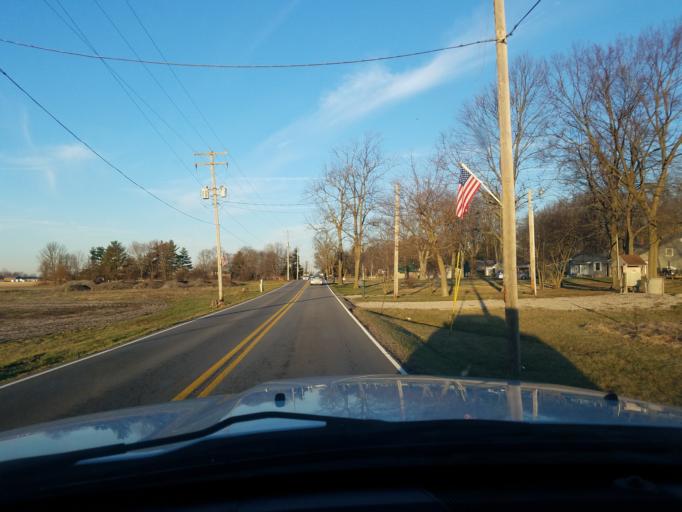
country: US
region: Indiana
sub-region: Johnson County
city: Whiteland
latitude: 39.5507
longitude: -86.0495
